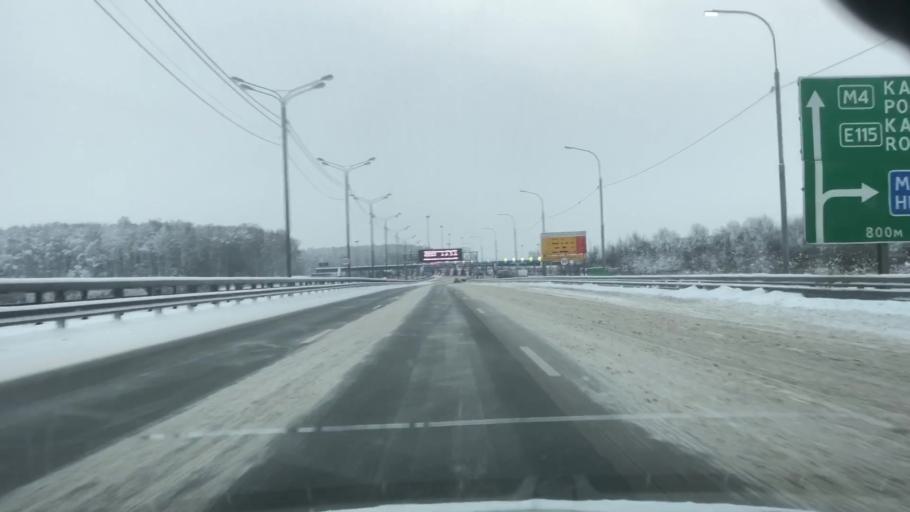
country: RU
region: Moskovskaya
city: Mikhnevo
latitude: 55.1724
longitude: 37.9139
